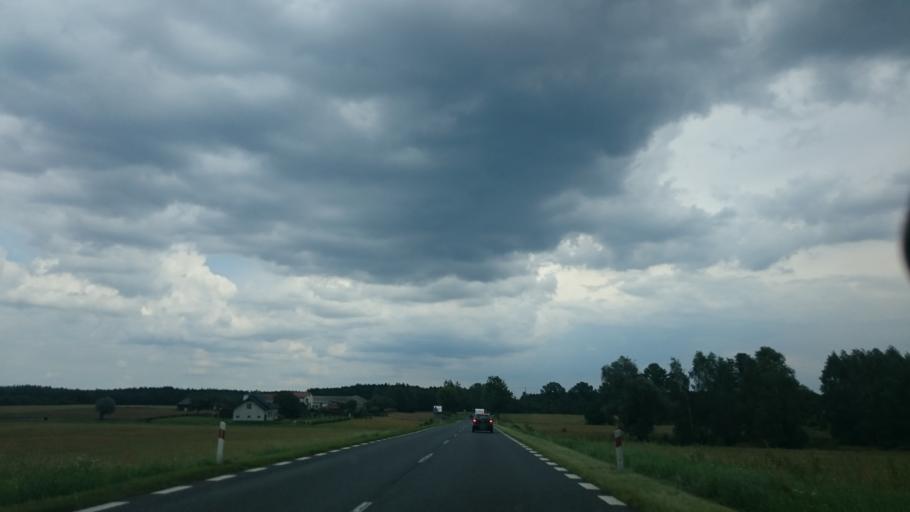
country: PL
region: Kujawsko-Pomorskie
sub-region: Powiat tucholski
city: Lubiewo
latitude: 53.4964
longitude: 18.0559
